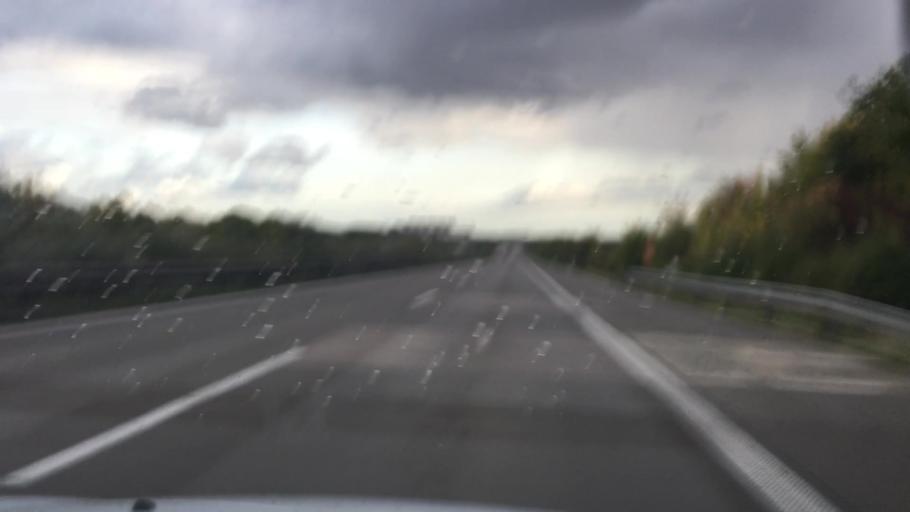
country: DE
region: Saxony-Anhalt
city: Welsleben
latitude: 52.0235
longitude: 11.6456
